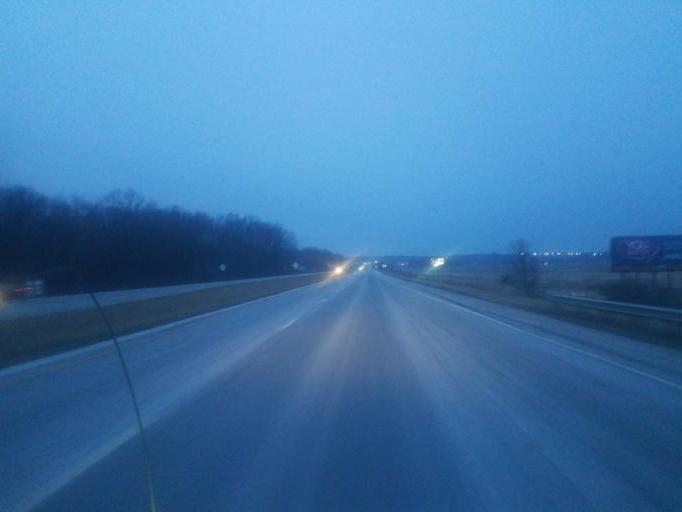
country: US
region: Ohio
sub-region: Wayne County
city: Wooster
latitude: 40.7934
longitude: -81.9550
